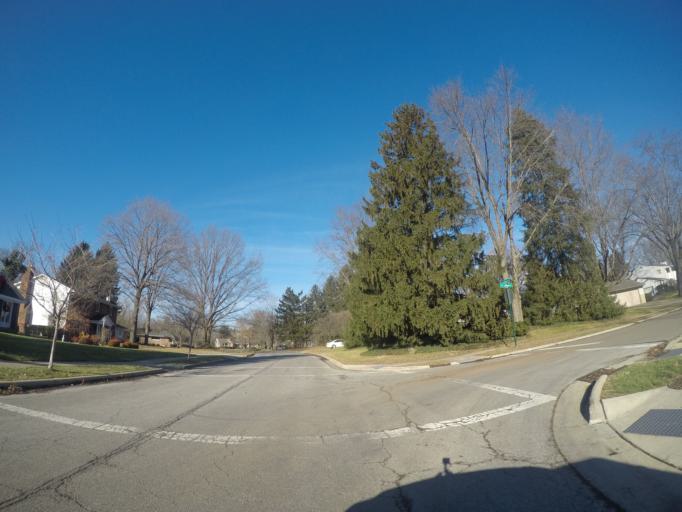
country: US
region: Ohio
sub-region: Franklin County
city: Upper Arlington
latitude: 40.0363
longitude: -83.0856
